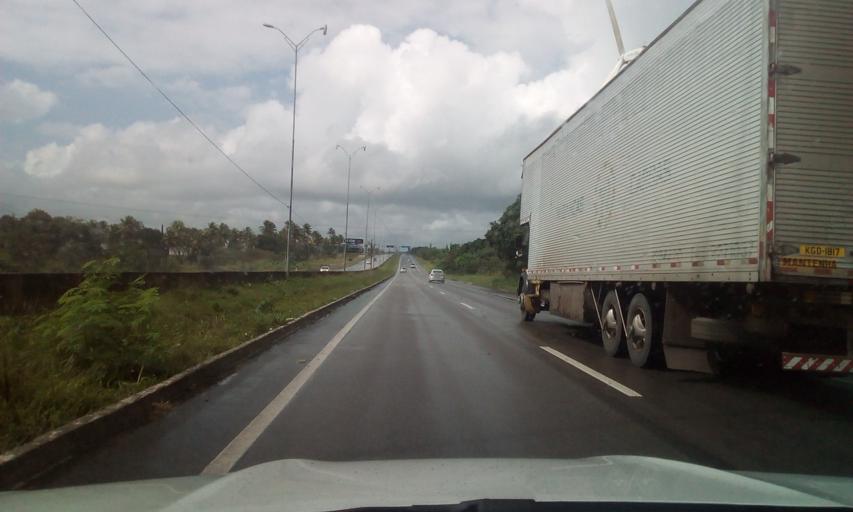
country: BR
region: Paraiba
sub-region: Conde
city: Conde
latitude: -7.2667
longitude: -34.9371
